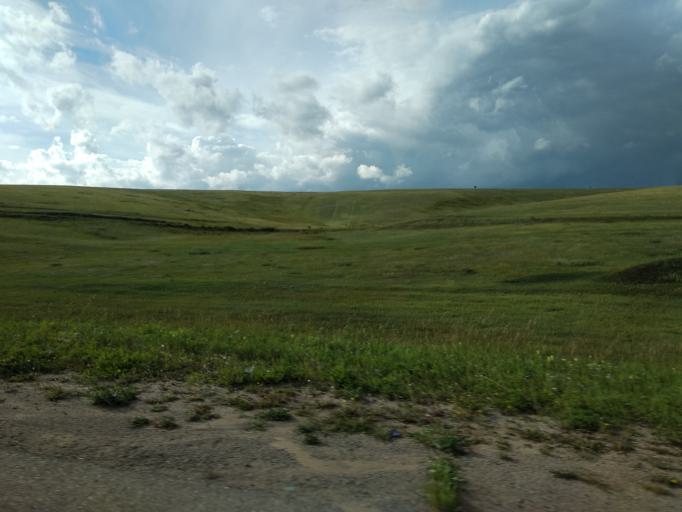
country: RU
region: Irkutsk
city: Bayanday
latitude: 52.9667
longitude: 105.3447
